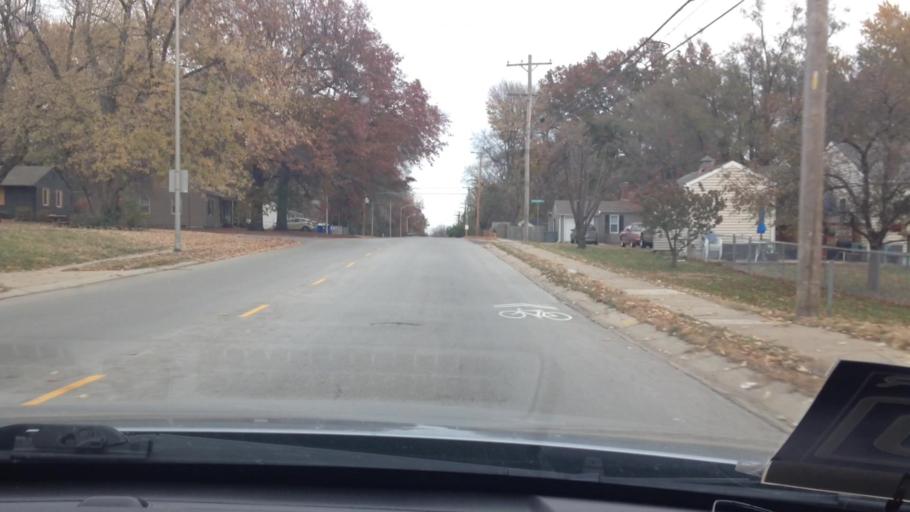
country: US
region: Kansas
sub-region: Johnson County
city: Overland Park
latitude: 39.0003
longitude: -94.6556
